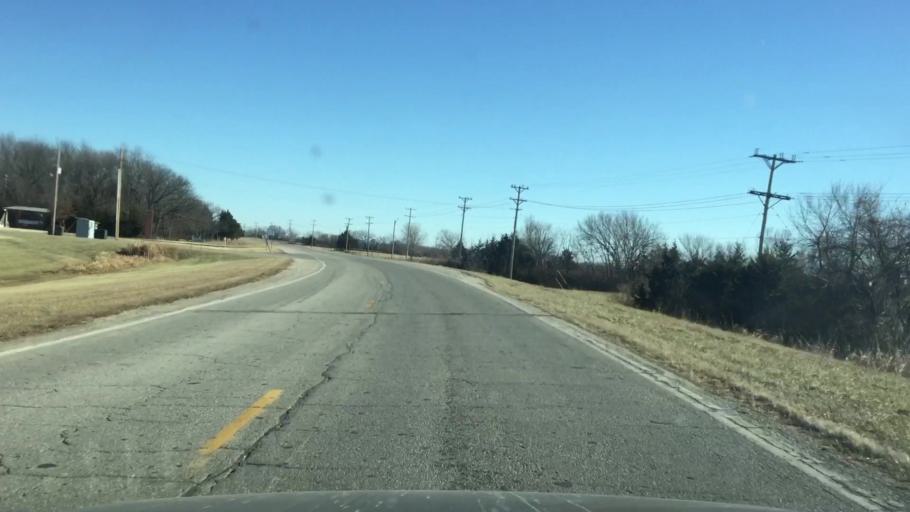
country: US
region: Kansas
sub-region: Allen County
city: Humboldt
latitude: 37.8205
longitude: -95.4304
